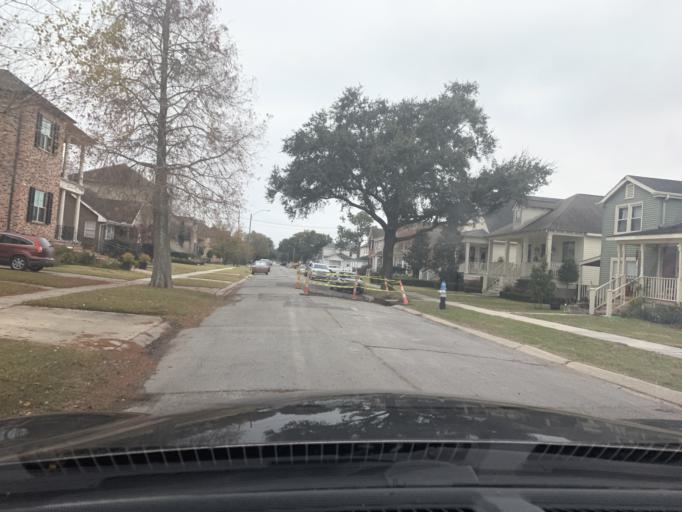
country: US
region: Louisiana
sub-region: Jefferson Parish
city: Metairie
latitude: 30.0083
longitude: -90.1110
